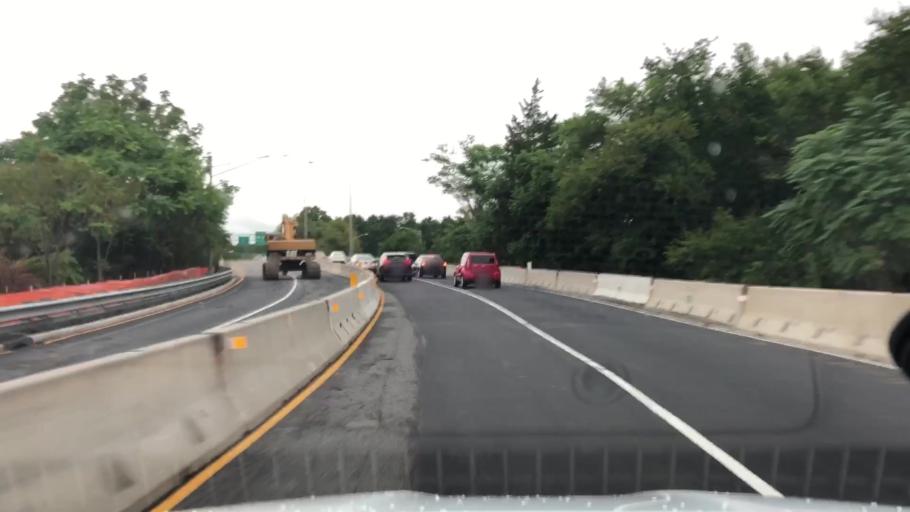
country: US
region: New Jersey
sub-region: Salem County
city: Carneys Point
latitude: 39.6778
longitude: -75.4850
